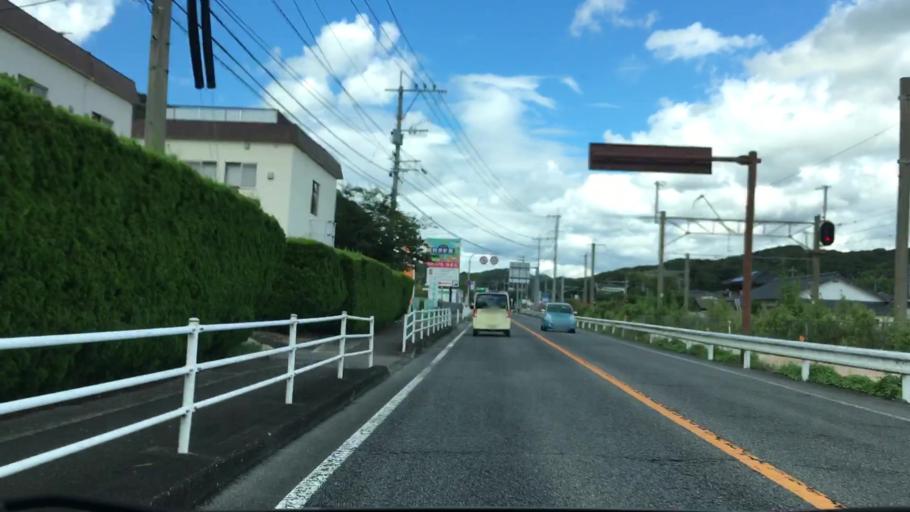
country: JP
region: Nagasaki
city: Sasebo
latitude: 33.1514
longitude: 129.8294
